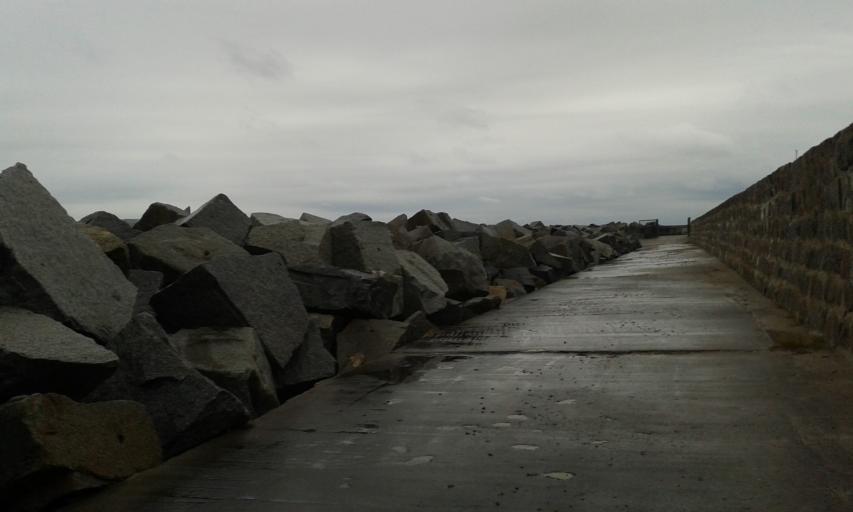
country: DE
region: Mecklenburg-Vorpommern
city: Sassnitz
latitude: 54.5123
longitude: 13.6471
